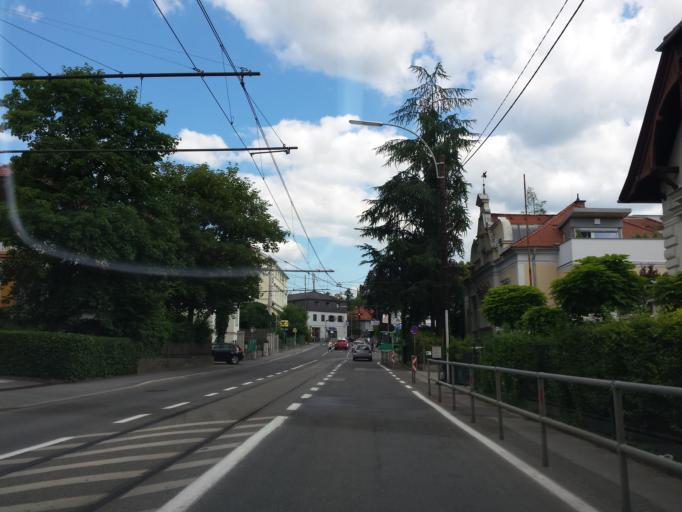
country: AT
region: Styria
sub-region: Graz Stadt
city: Graz
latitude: 47.0887
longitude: 15.4600
